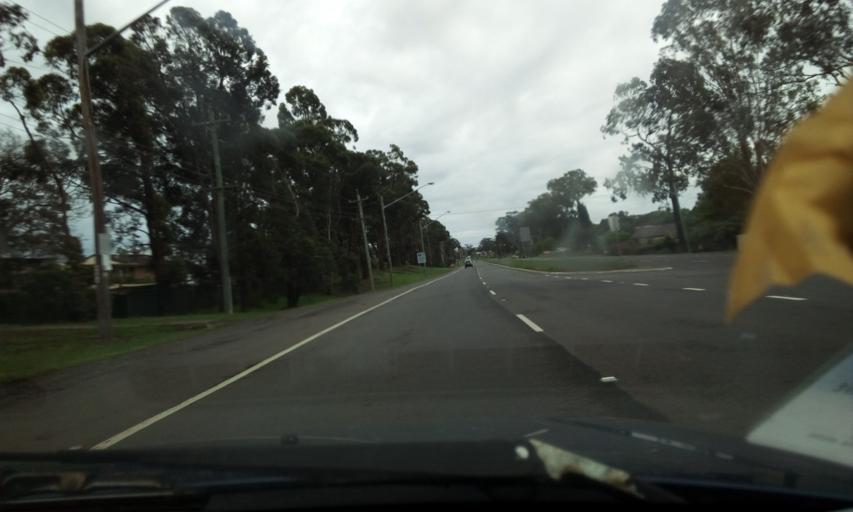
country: AU
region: New South Wales
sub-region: Camden
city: Camden South
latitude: -34.0826
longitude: 150.6946
